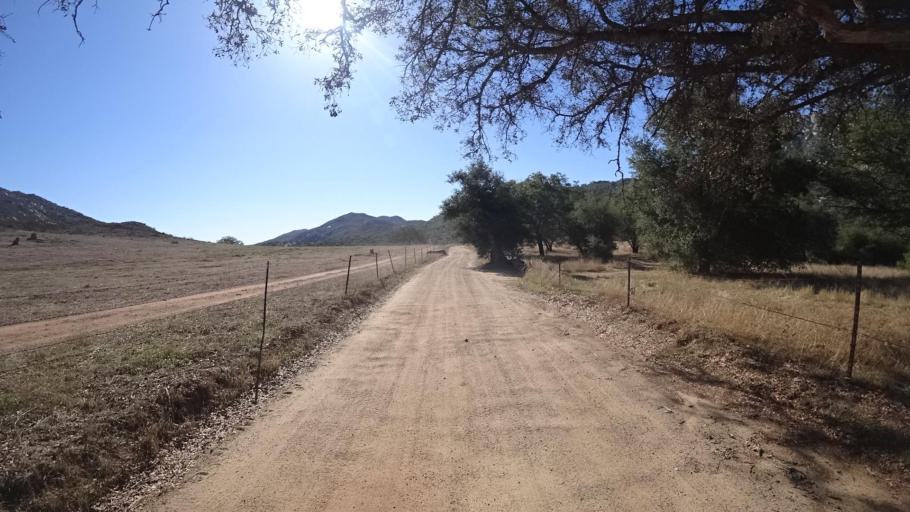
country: US
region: California
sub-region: San Diego County
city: Alpine
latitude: 32.7171
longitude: -116.7564
